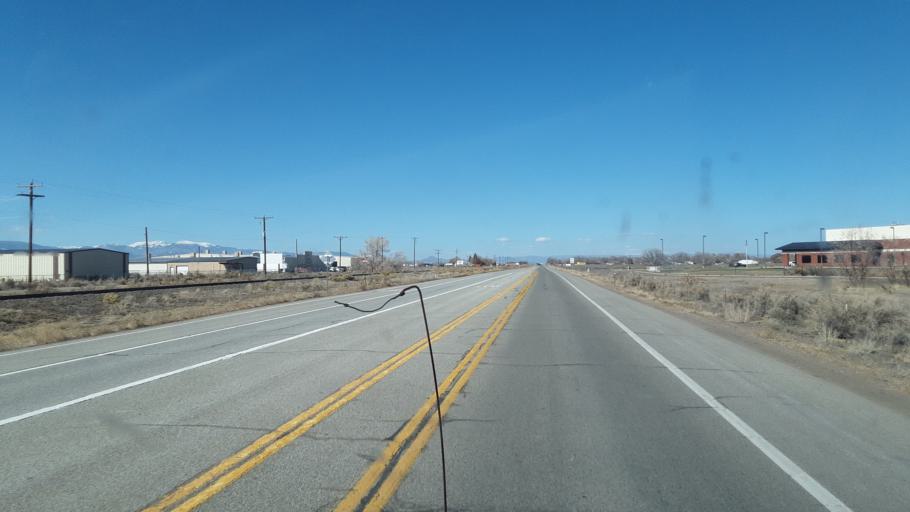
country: US
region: Colorado
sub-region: Alamosa County
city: Alamosa
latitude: 37.4905
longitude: -105.9308
